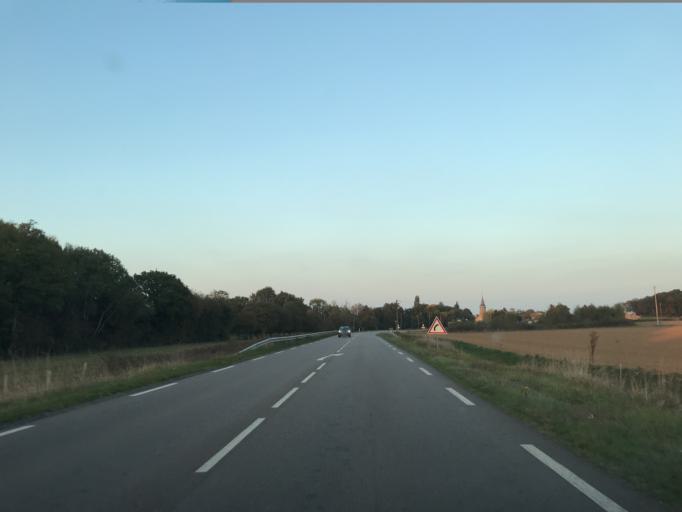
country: FR
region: Haute-Normandie
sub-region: Departement de l'Eure
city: Bourth
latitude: 48.6814
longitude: 0.8024
